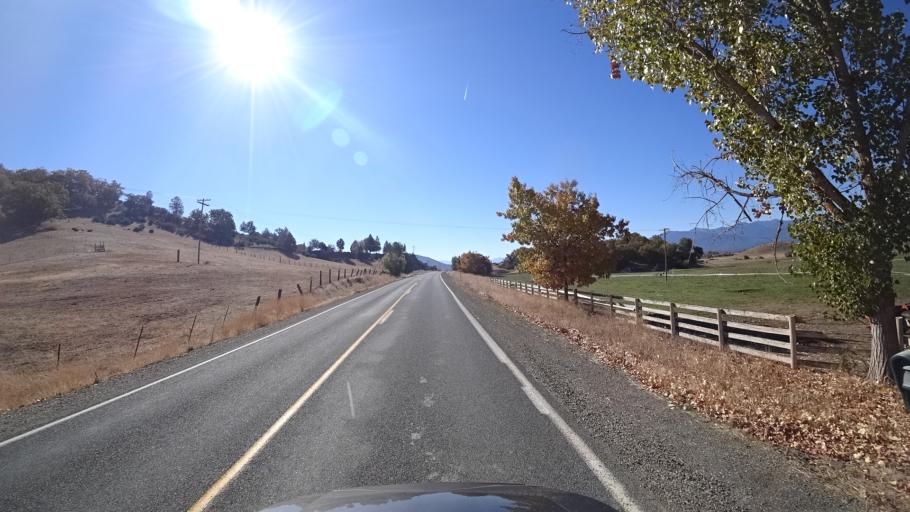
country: US
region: California
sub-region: Siskiyou County
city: Yreka
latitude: 41.5882
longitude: -122.8363
